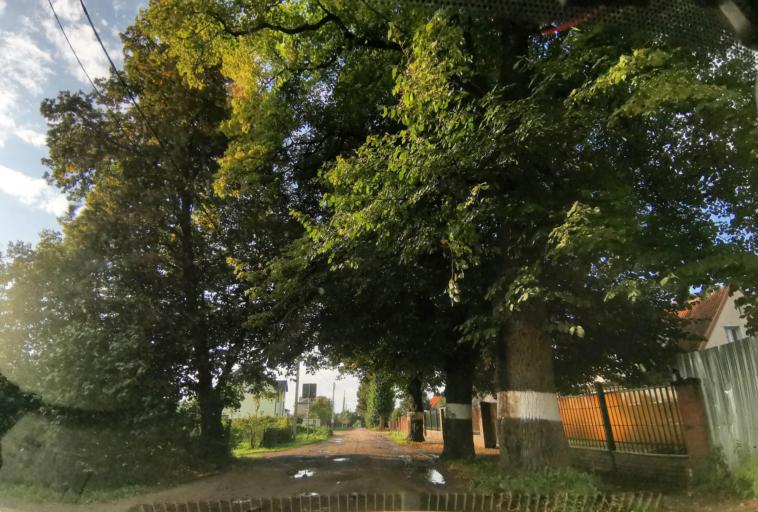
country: RU
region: Kaliningrad
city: Chernyakhovsk
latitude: 54.6560
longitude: 21.8381
